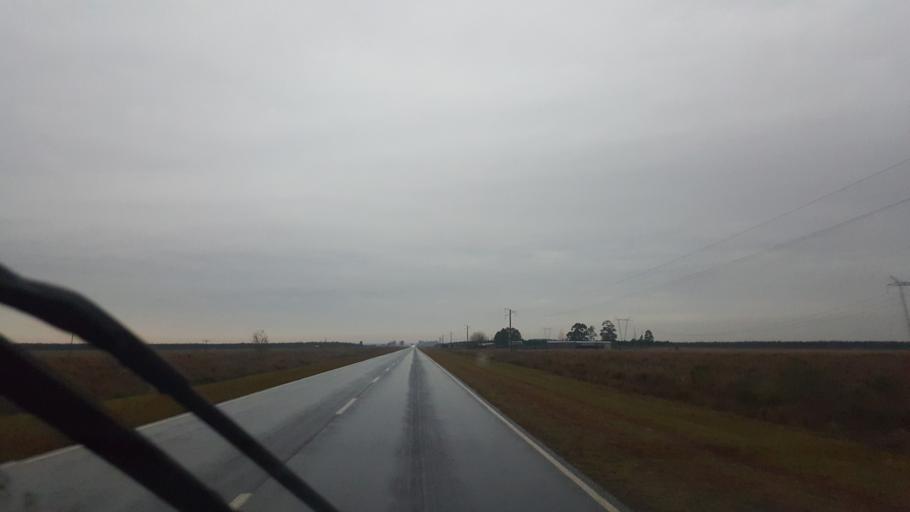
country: PY
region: Itapua
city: San Cosme y Damian
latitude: -27.5570
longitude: -56.2402
